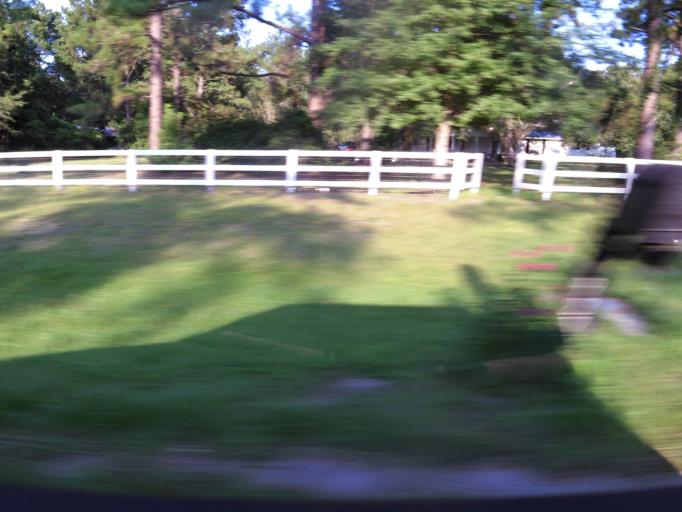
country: US
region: Florida
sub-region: Duval County
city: Baldwin
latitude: 30.3951
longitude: -82.0311
